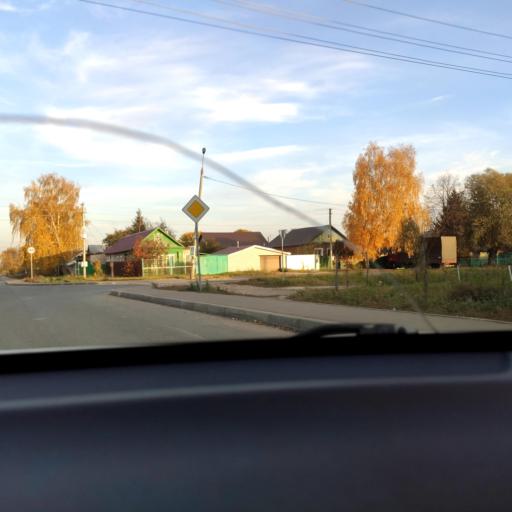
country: RU
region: Tatarstan
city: Staroye Arakchino
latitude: 55.8791
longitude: 49.0473
